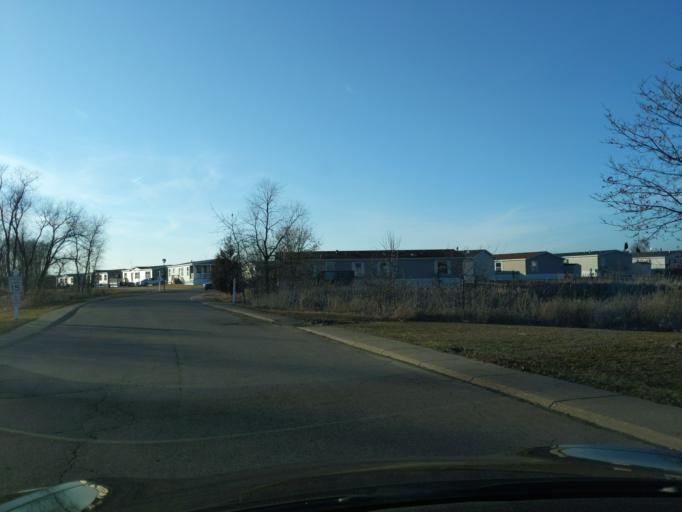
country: US
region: Michigan
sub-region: Jackson County
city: Jackson
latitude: 42.2787
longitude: -84.4748
